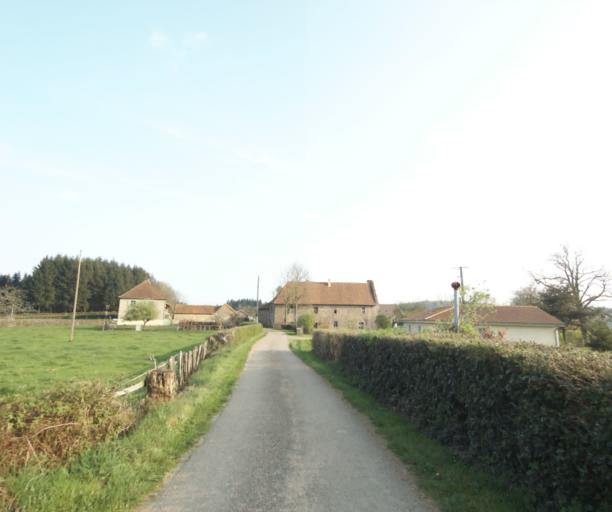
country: FR
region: Bourgogne
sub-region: Departement de Saone-et-Loire
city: Matour
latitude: 46.4275
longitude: 4.4816
